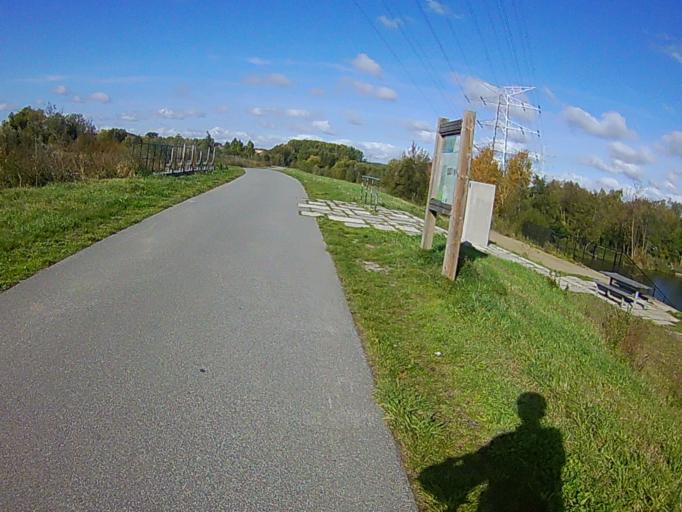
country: BE
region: Flanders
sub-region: Provincie Antwerpen
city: Niel
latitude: 51.1277
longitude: 4.3053
